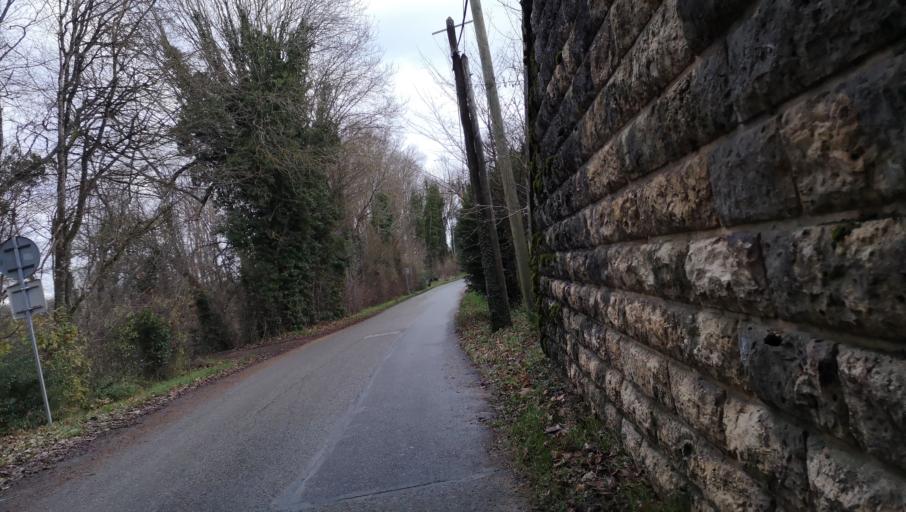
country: FR
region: Centre
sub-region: Departement du Loiret
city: Saint-Jean-de-Braye
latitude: 47.9088
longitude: 1.9991
